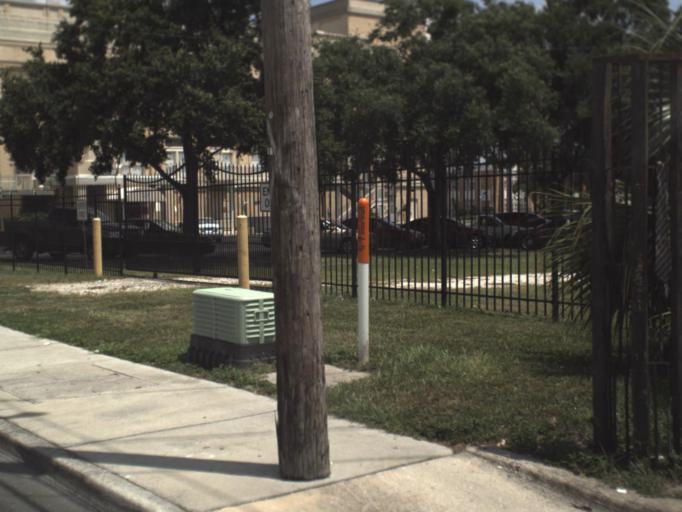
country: US
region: Florida
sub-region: Hillsborough County
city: Tampa
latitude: 27.9613
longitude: -82.4512
